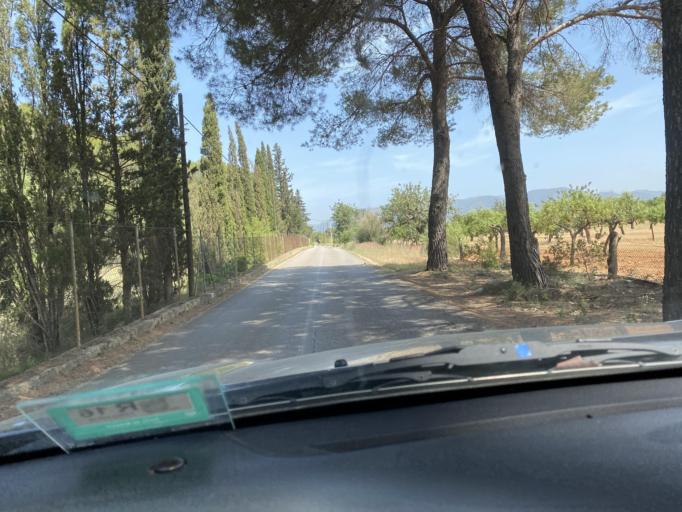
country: ES
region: Balearic Islands
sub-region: Illes Balears
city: Marratxi
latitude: 39.6274
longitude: 2.7112
